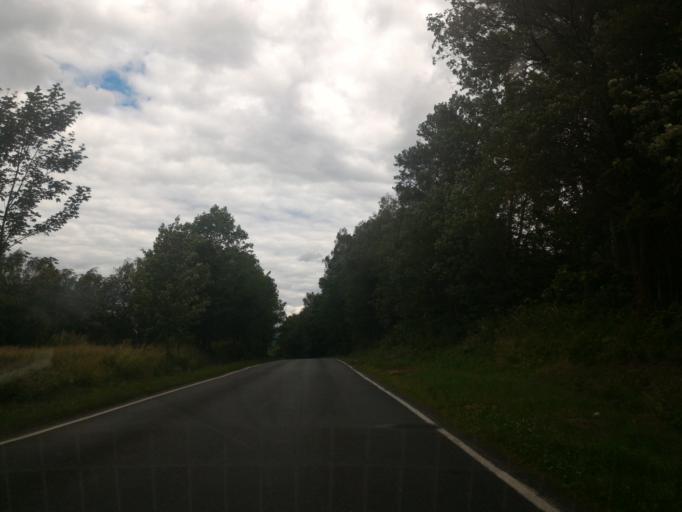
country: CZ
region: Vysocina
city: Ledec nad Sazavou
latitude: 49.6458
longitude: 15.2680
